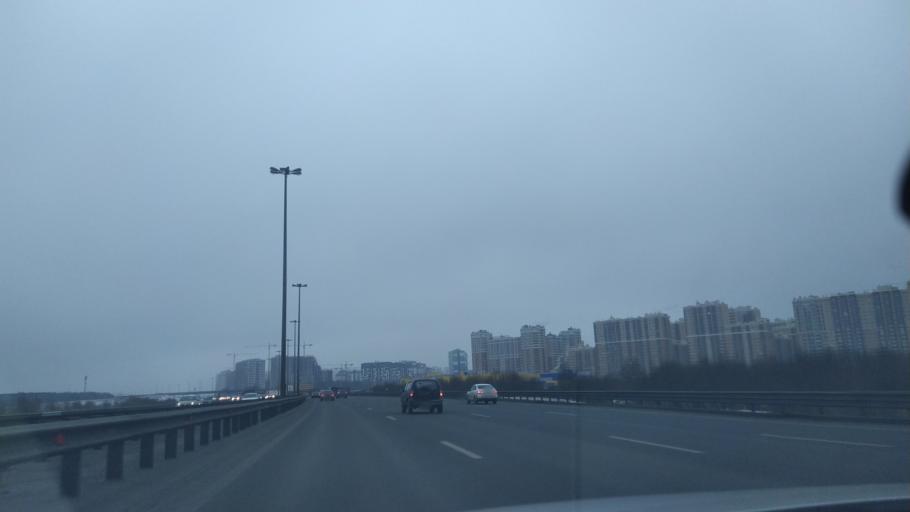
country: RU
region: St.-Petersburg
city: Krasnogvargeisky
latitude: 59.9220
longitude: 30.5276
